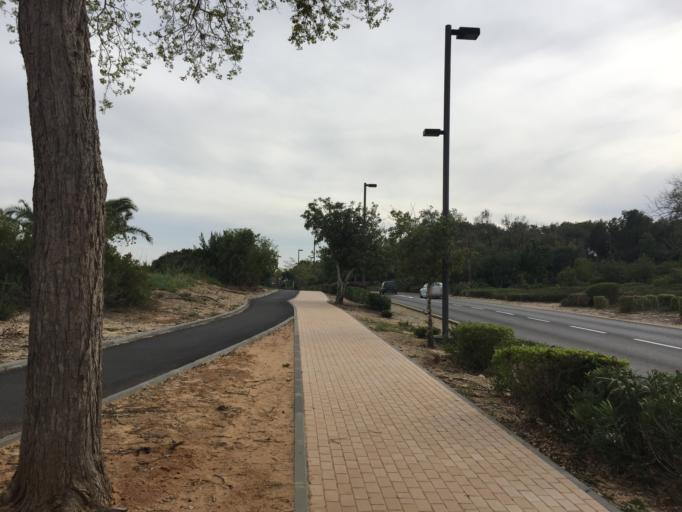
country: IL
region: Haifa
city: Qesarya
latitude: 32.5085
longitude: 34.9040
